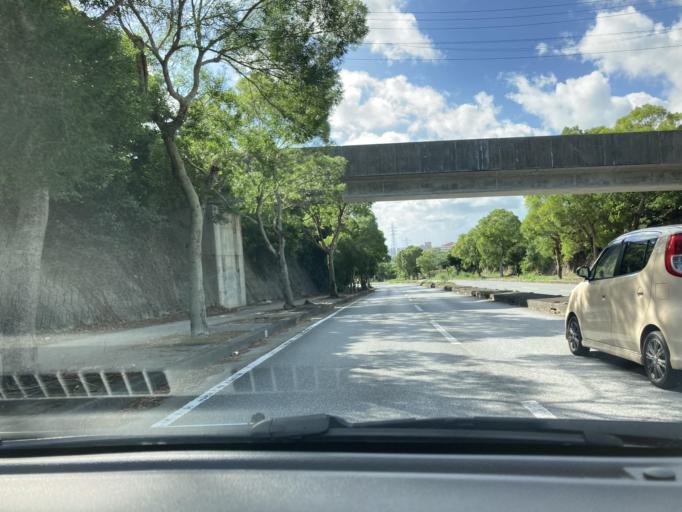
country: JP
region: Okinawa
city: Itoman
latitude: 26.1525
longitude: 127.6812
